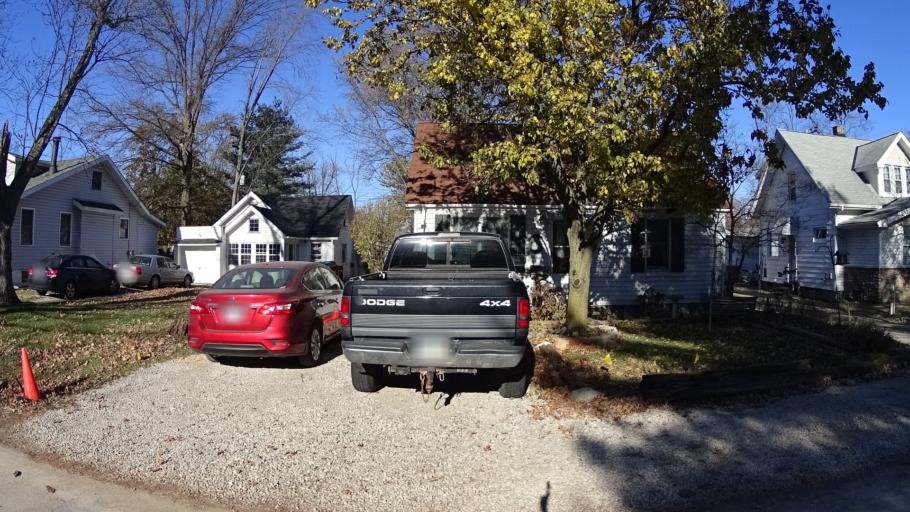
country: US
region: Ohio
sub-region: Lorain County
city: Avon Lake
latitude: 41.5075
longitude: -81.9841
